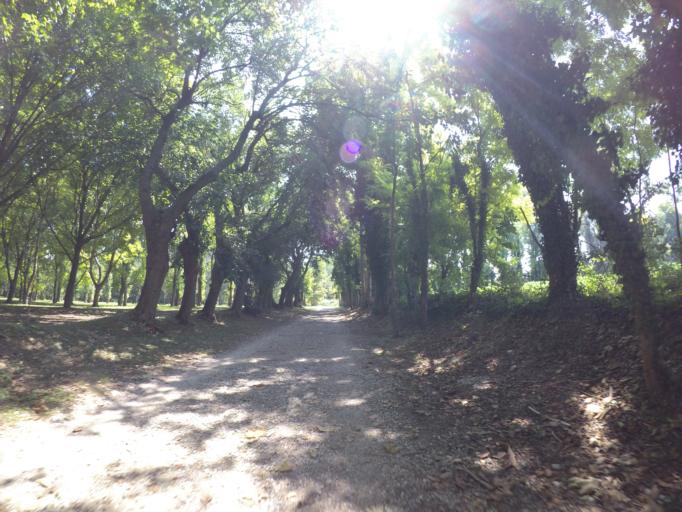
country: IT
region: Friuli Venezia Giulia
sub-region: Provincia di Udine
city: Codroipo
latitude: 45.9532
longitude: 12.9789
